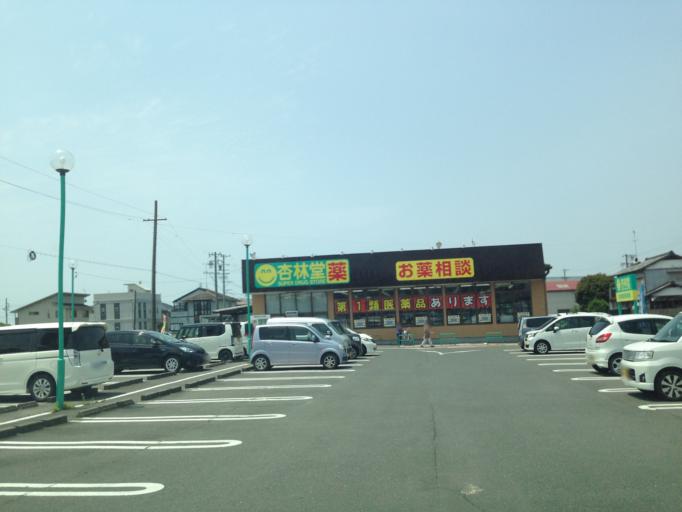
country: JP
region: Shizuoka
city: Fukuroi
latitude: 34.7419
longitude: 137.9131
